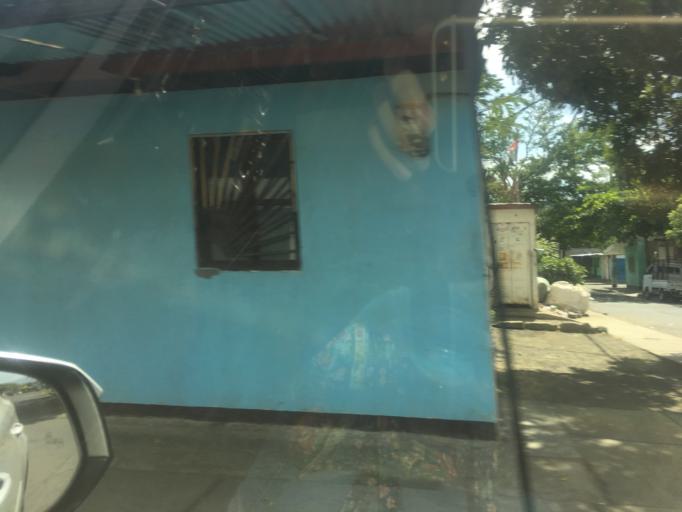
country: NI
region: Managua
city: Managua
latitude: 12.1560
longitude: -86.2766
